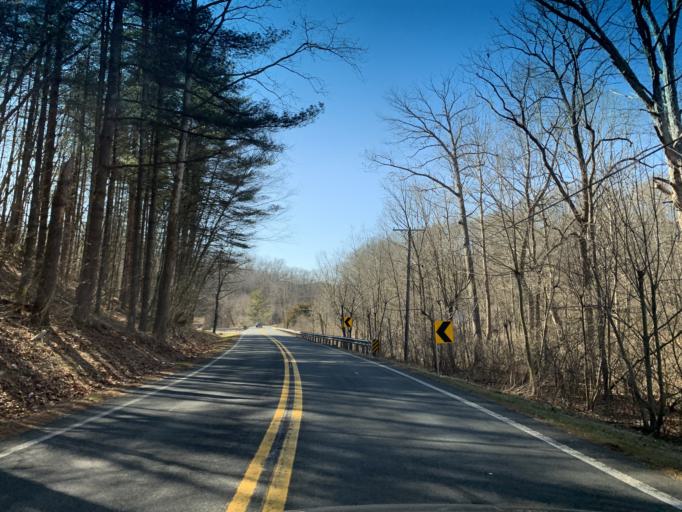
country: US
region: Maryland
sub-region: Carroll County
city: Hampstead
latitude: 39.5758
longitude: -76.8927
